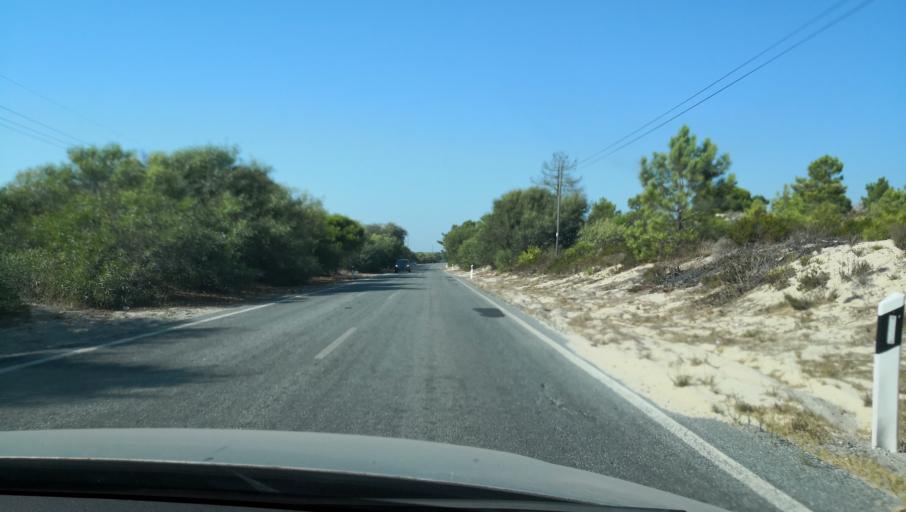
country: PT
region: Setubal
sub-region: Setubal
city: Setubal
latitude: 38.3949
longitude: -8.8041
